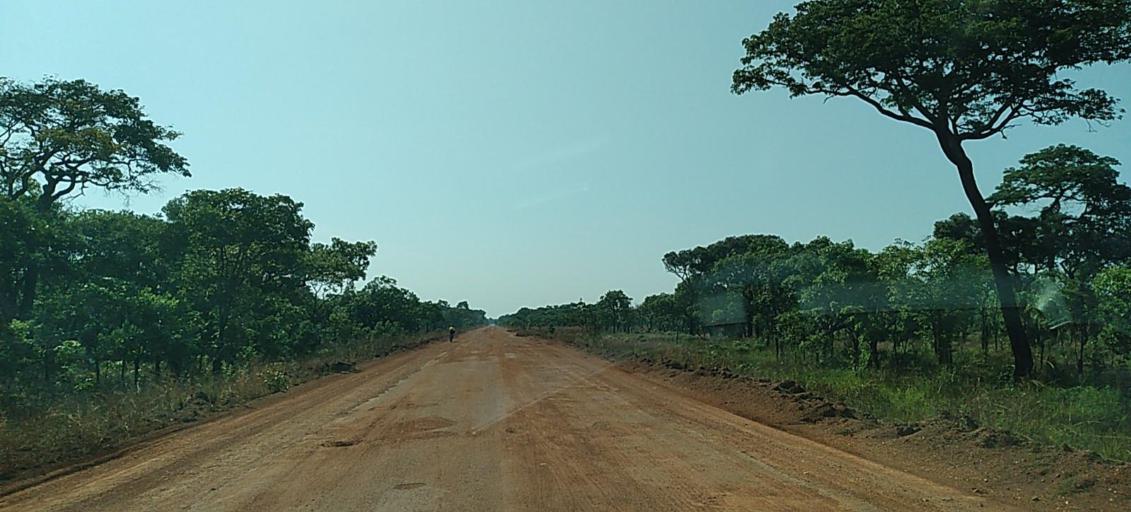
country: ZM
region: North-Western
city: Mwinilunga
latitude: -11.9113
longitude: 25.2988
